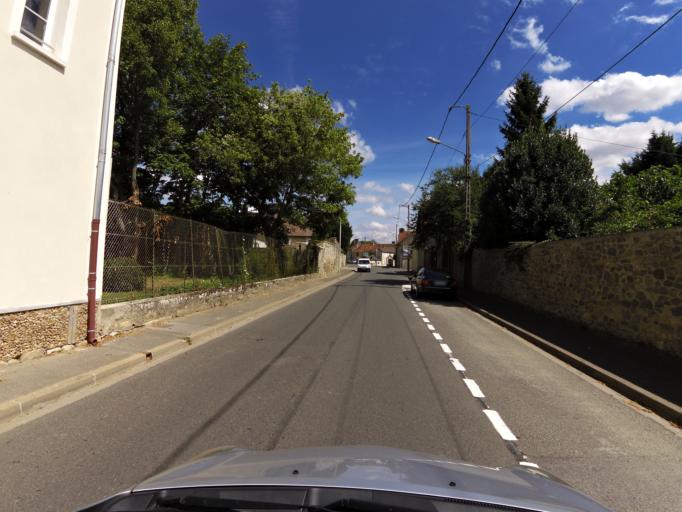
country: FR
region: Ile-de-France
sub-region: Departement de Seine-et-Marne
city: Lizy-sur-Ourcq
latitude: 49.0735
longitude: 3.0232
